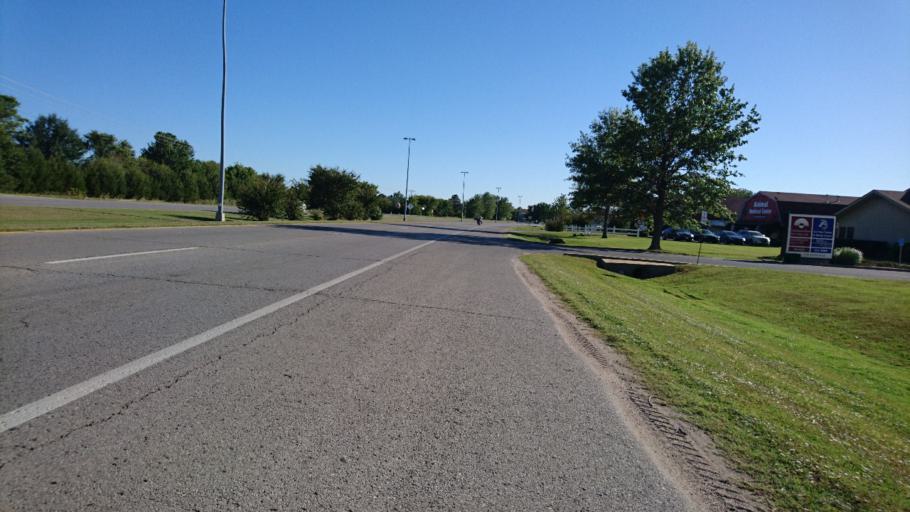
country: US
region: Oklahoma
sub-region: Rogers County
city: Claremore
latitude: 36.3282
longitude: -95.6065
